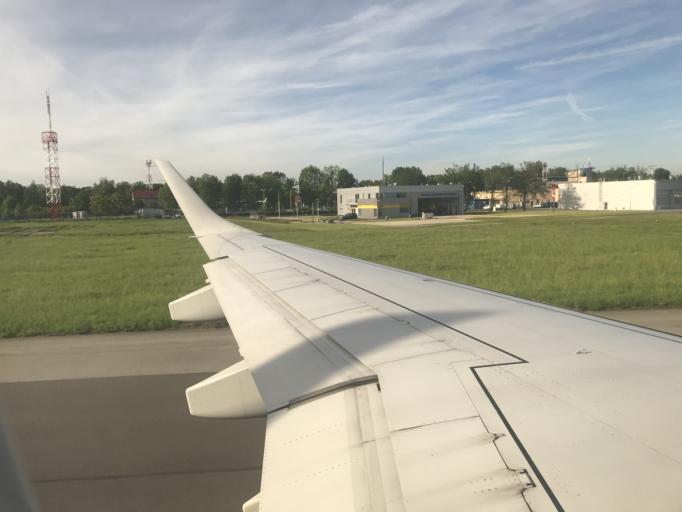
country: PL
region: Lower Silesian Voivodeship
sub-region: Powiat wroclawski
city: Smolec
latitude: 51.1029
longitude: 16.8966
